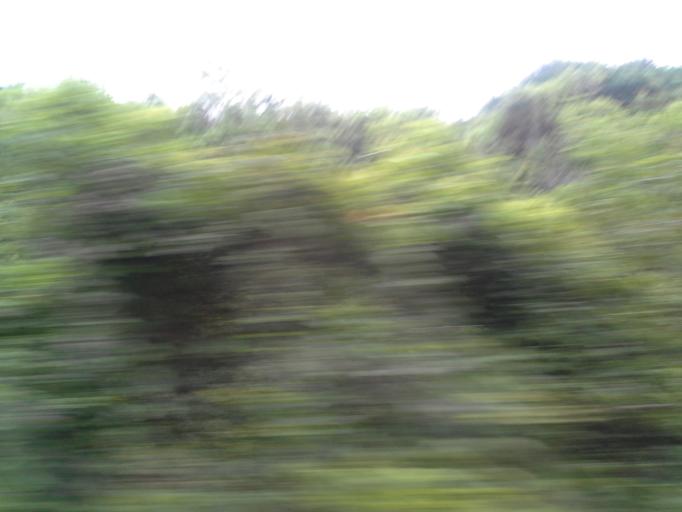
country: CO
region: Sucre
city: Ovejas
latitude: 9.5037
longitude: -75.1552
